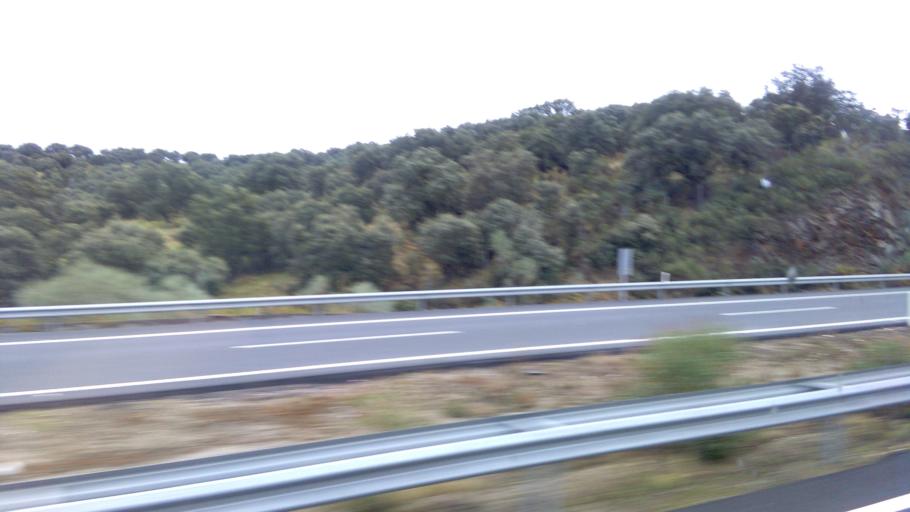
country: ES
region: Extremadura
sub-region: Provincia de Caceres
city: Almaraz
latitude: 39.8026
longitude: -5.6738
